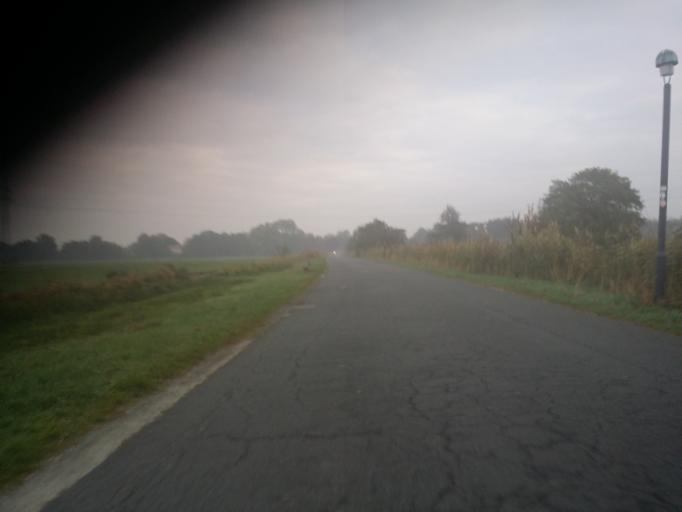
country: DE
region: Lower Saxony
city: Lilienthal
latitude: 53.1256
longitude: 8.8600
